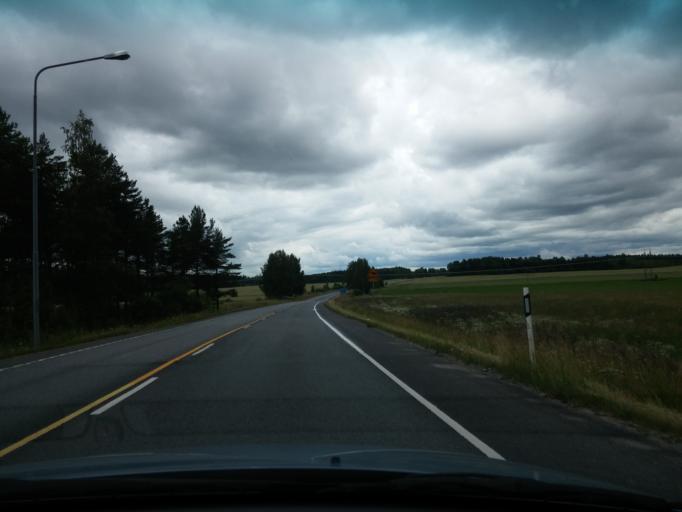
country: FI
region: Uusimaa
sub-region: Porvoo
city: Porvoo
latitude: 60.3940
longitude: 25.6048
